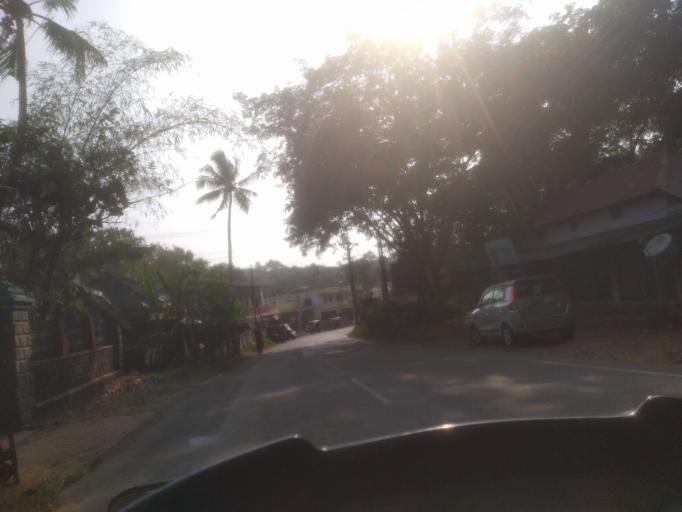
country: IN
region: Kerala
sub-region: Ernakulam
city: Piravam
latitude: 9.8344
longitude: 76.5200
